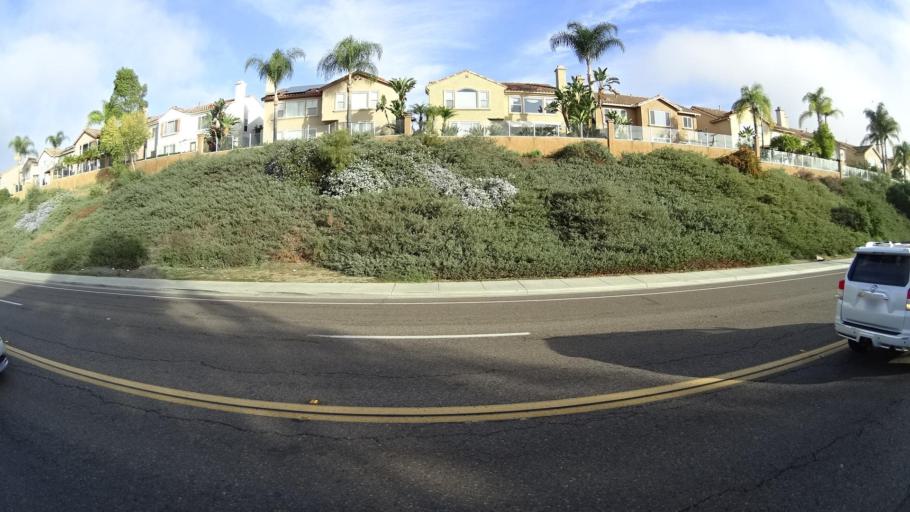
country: US
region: California
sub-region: San Diego County
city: Rancho San Diego
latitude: 32.7428
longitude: -116.9222
